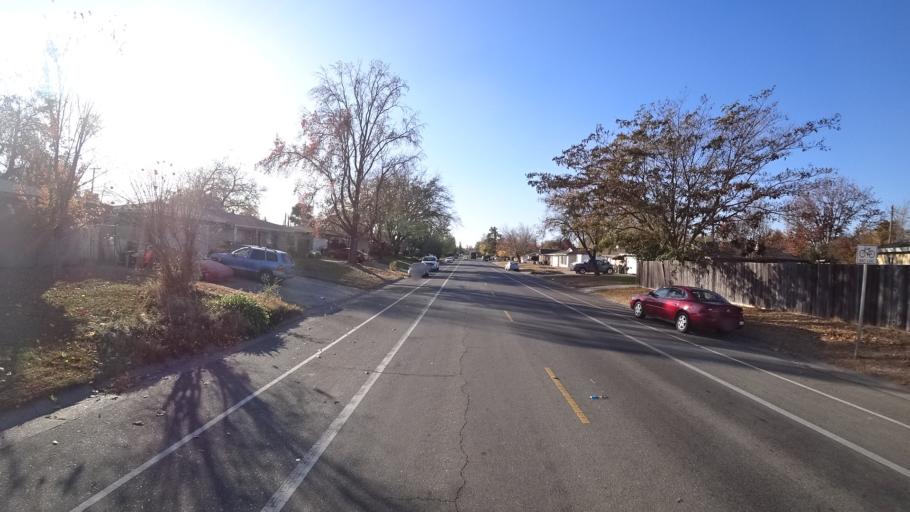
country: US
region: California
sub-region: Sacramento County
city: Citrus Heights
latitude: 38.6988
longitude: -121.3005
